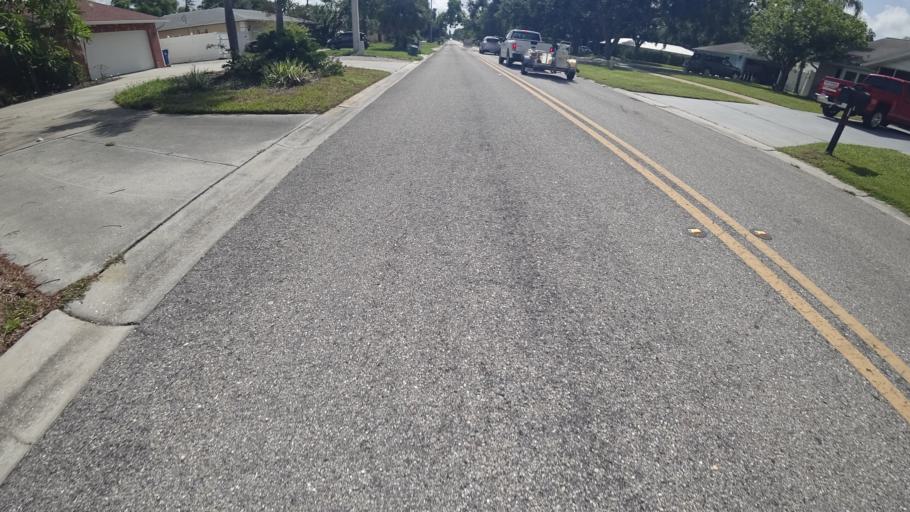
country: US
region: Florida
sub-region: Manatee County
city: West Bradenton
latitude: 27.5145
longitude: -82.6431
